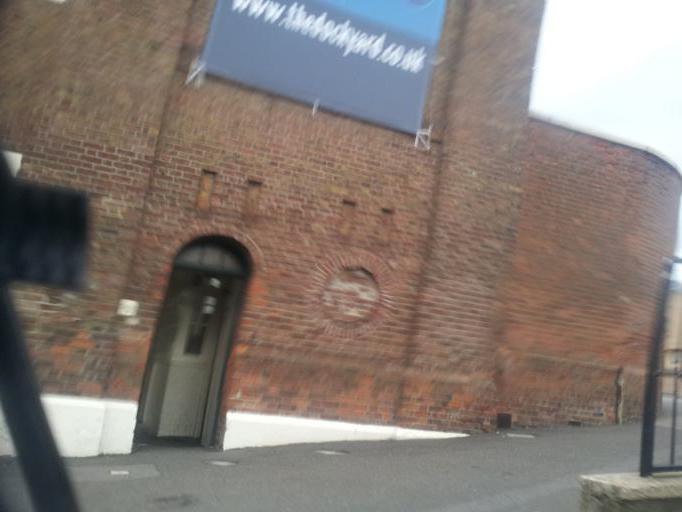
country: GB
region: England
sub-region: Kent
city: Chatham
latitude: 51.3916
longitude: 0.5266
